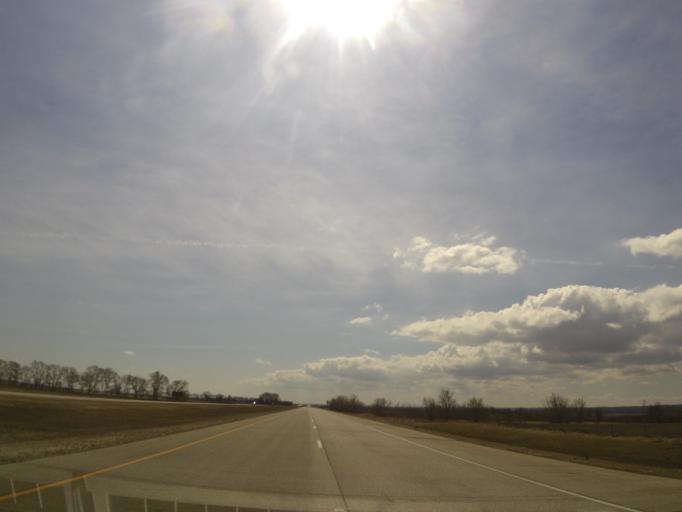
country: US
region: South Dakota
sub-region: Roberts County
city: Sisseton
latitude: 45.6126
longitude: -96.9896
